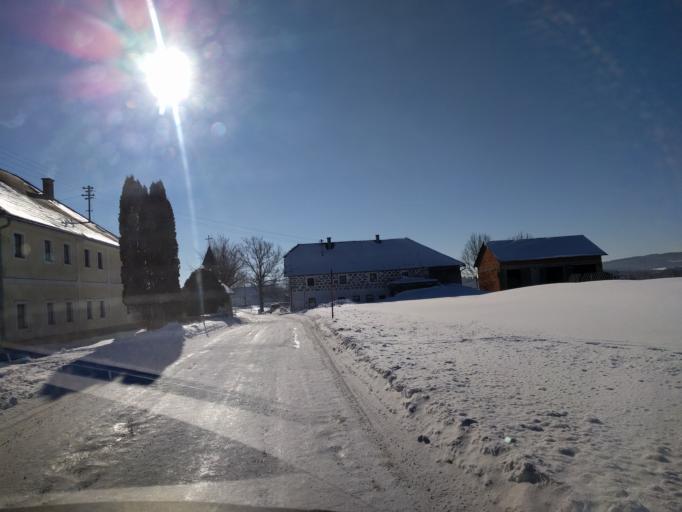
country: AT
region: Upper Austria
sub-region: Politischer Bezirk Urfahr-Umgebung
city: Zwettl an der Rodl
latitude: 48.4906
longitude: 14.2785
